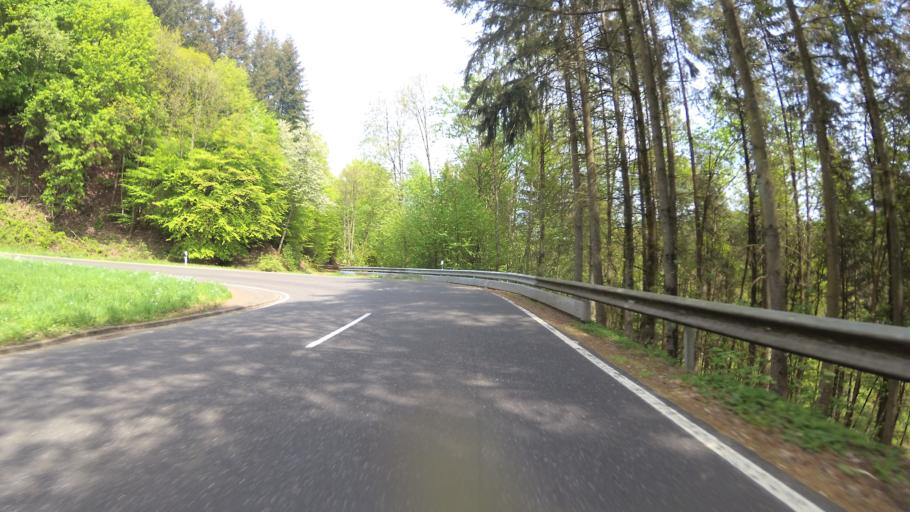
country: DE
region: Rheinland-Pfalz
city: Bausendorf
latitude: 50.0329
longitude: 6.9977
